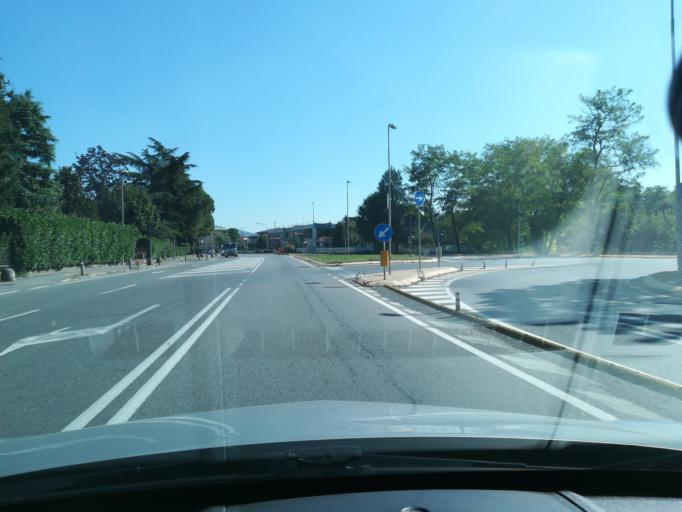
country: IT
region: Lombardy
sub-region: Provincia di Bergamo
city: Montello
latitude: 45.6761
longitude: 9.8014
